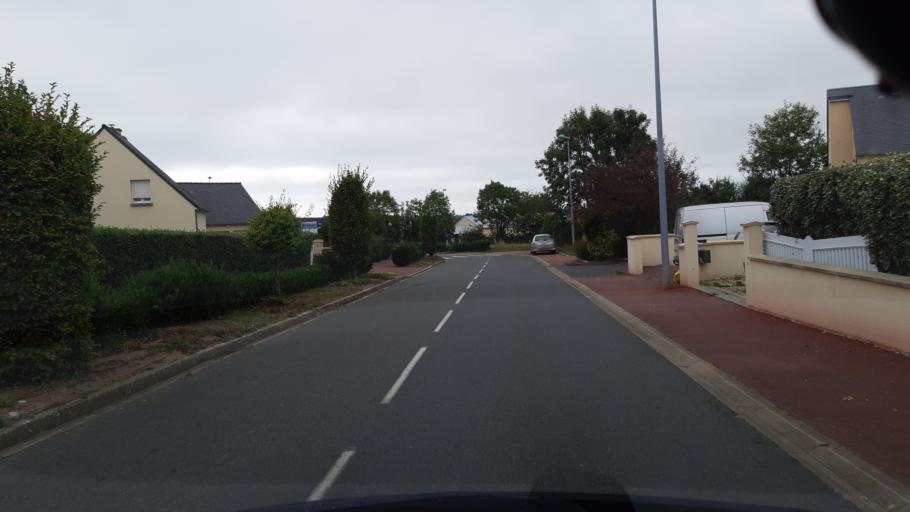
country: FR
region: Lower Normandy
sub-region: Departement de la Manche
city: Donville-les-Bains
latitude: 48.8401
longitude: -1.5580
